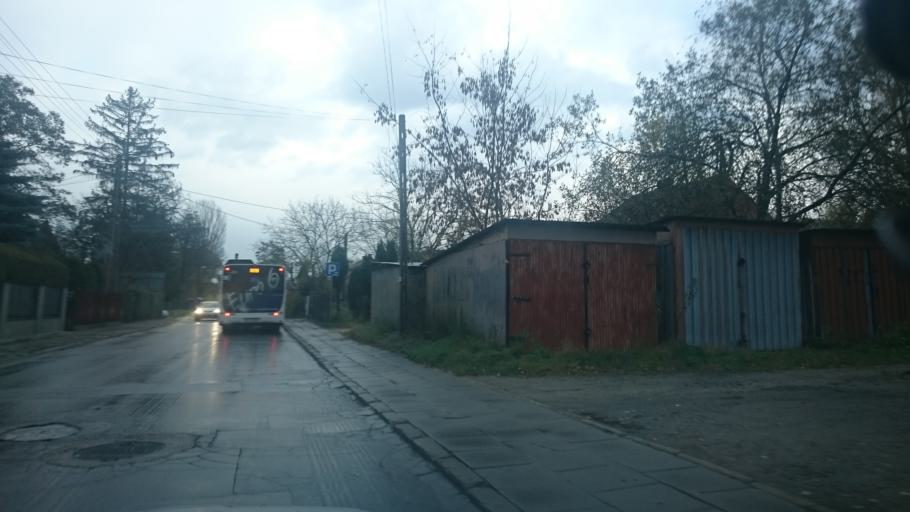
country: PL
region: Lesser Poland Voivodeship
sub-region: Powiat wielicki
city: Czarnochowice
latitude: 50.0223
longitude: 20.0055
